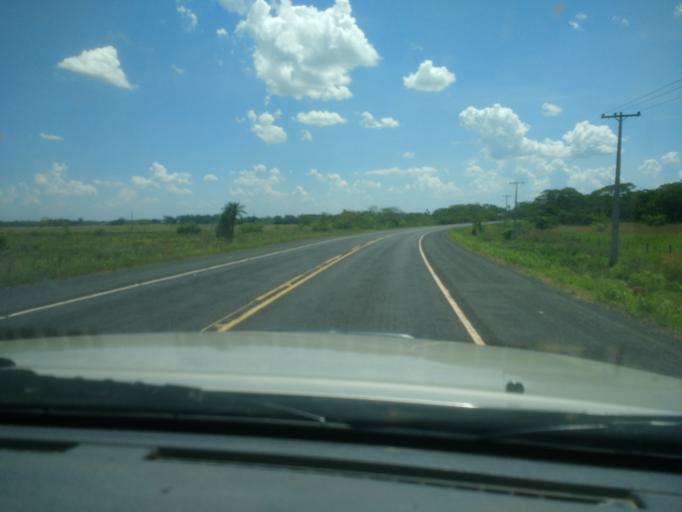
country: PY
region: San Pedro
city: Itacurubi del Rosario
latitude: -24.5261
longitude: -56.8355
